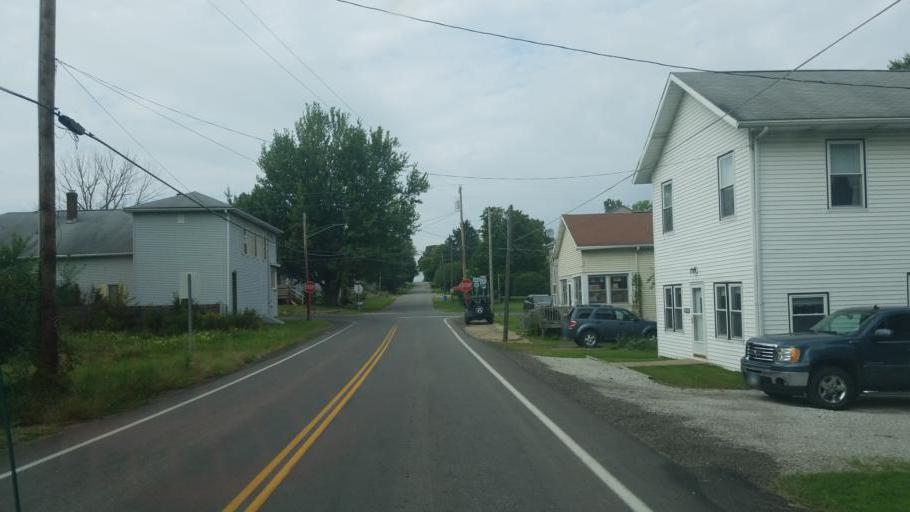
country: US
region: Ohio
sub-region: Wayne County
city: West Salem
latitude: 40.9254
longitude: -82.0522
